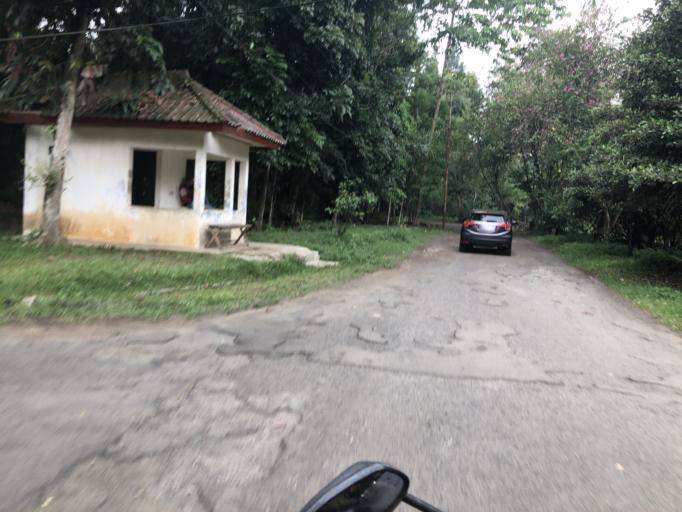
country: ID
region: West Java
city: Ciampea
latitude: -6.5534
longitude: 106.7217
